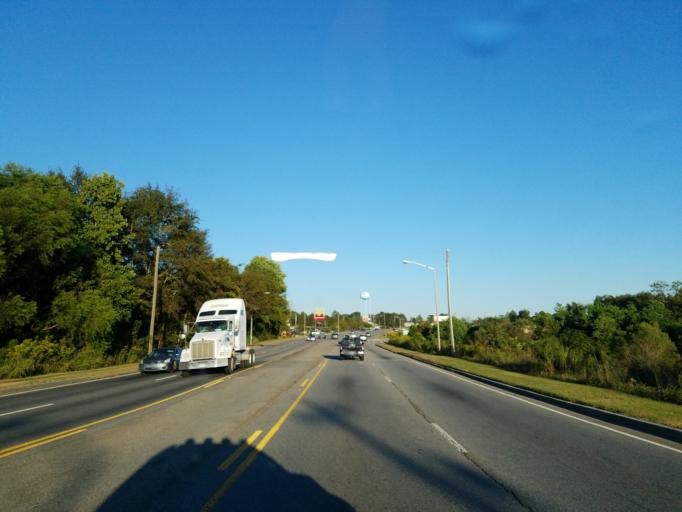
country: US
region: Georgia
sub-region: Worth County
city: Sylvester
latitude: 31.5302
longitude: -83.8290
